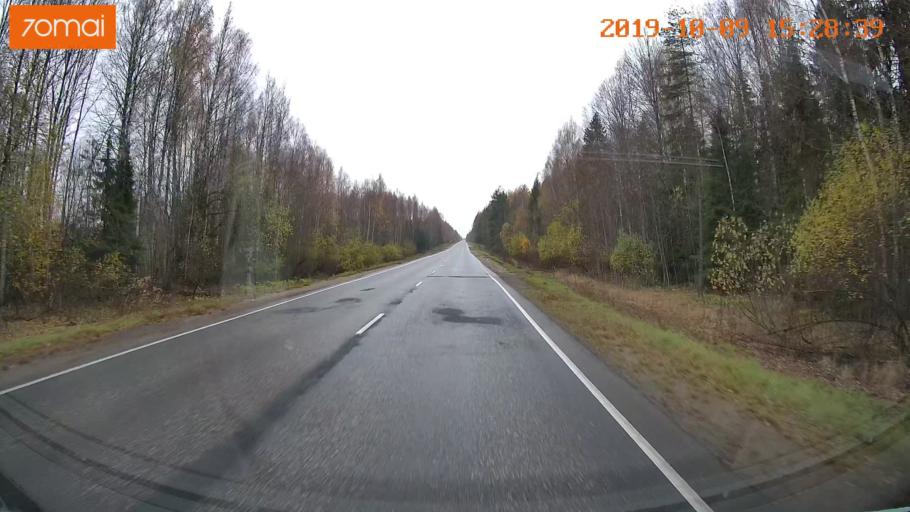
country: RU
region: Kostroma
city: Susanino
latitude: 58.0006
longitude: 41.3564
